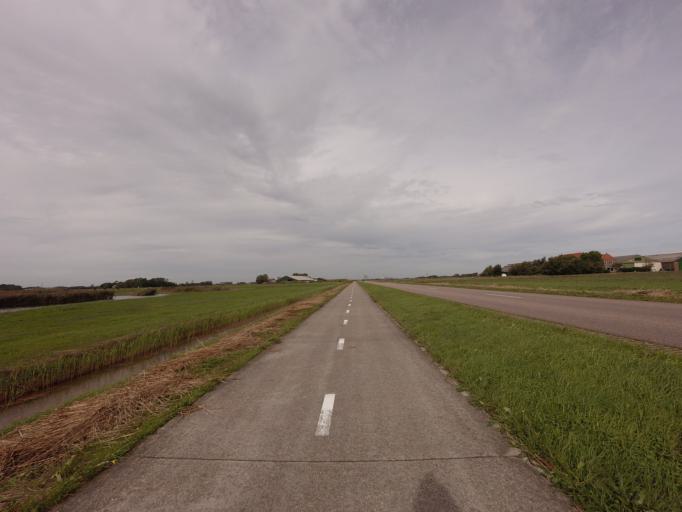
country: NL
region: North Holland
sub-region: Gemeente Texel
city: Den Burg
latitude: 53.0468
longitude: 4.8497
